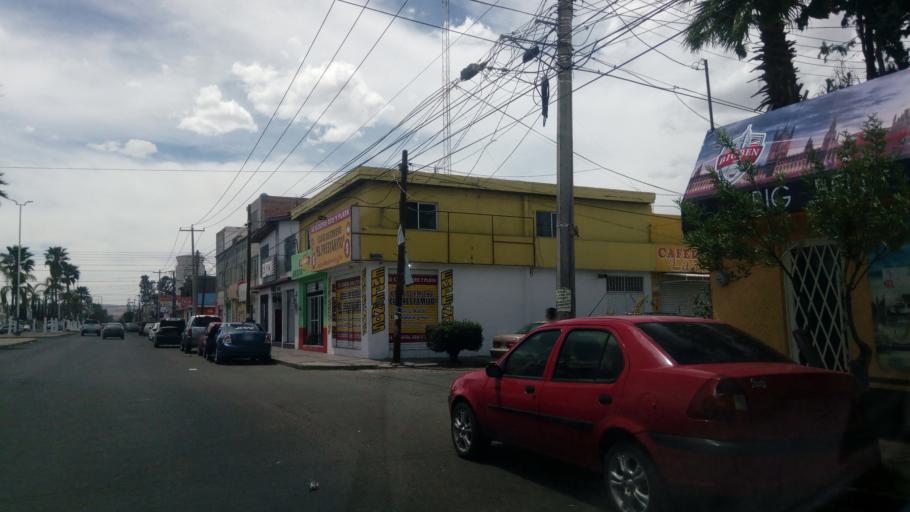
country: MX
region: Durango
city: Victoria de Durango
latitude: 23.9958
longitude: -104.6638
